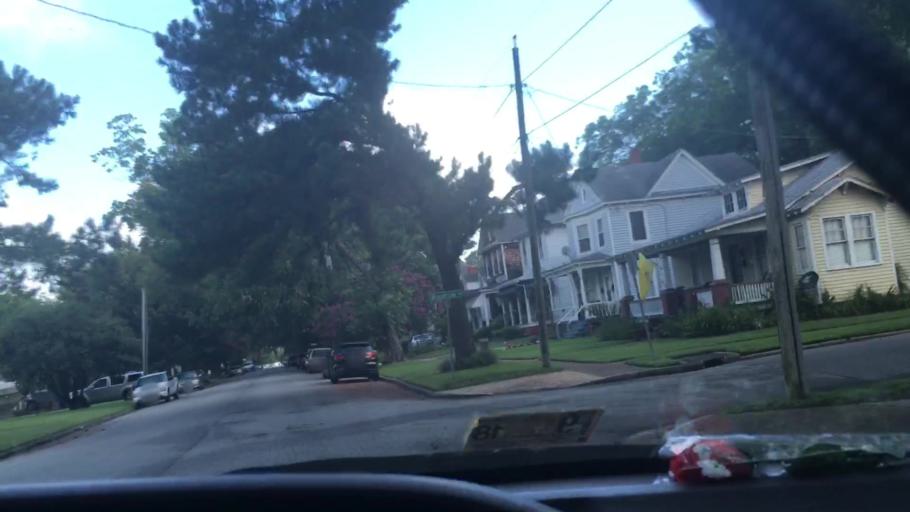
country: US
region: Virginia
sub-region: City of Portsmouth
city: Portsmouth Heights
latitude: 36.8445
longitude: -76.3376
